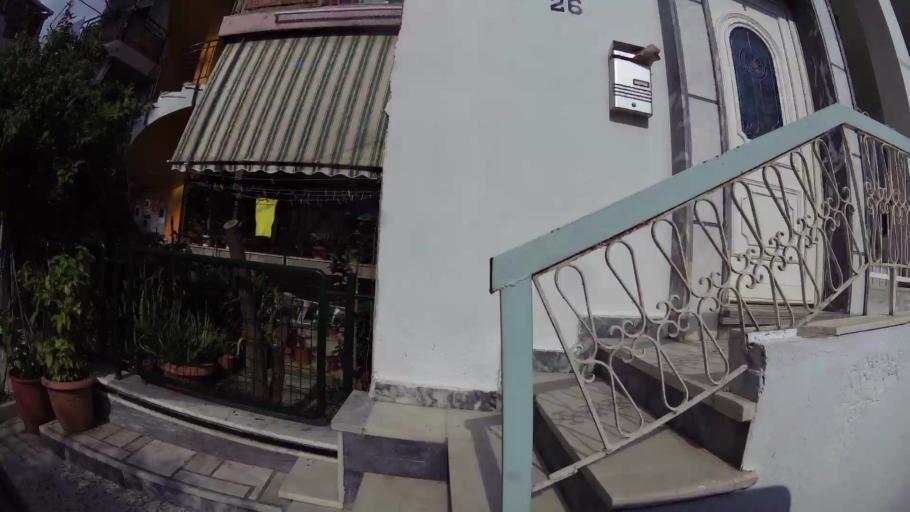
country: GR
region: Attica
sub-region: Nomarchia Athinas
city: Irakleio
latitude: 38.0523
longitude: 23.7560
